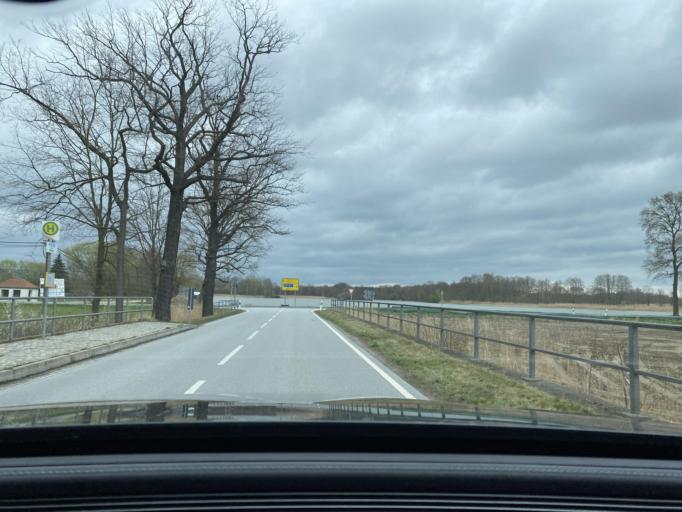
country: DE
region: Saxony
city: Neschwitz
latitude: 51.2666
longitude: 14.3436
